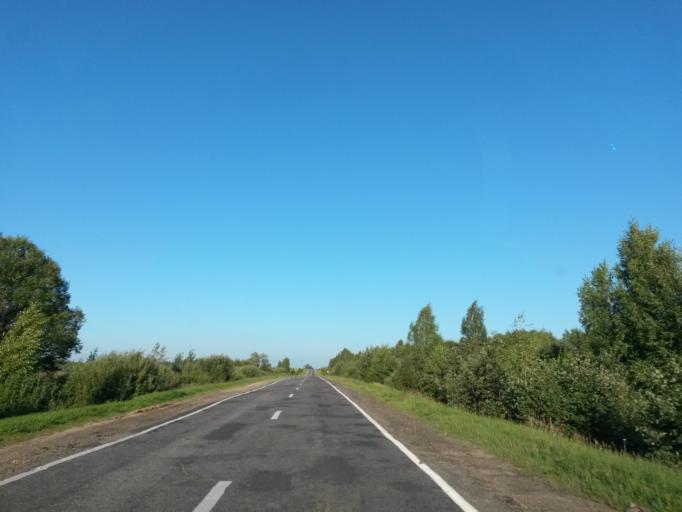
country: RU
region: Jaroslavl
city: Gavrilov-Yam
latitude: 57.3079
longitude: 39.9062
